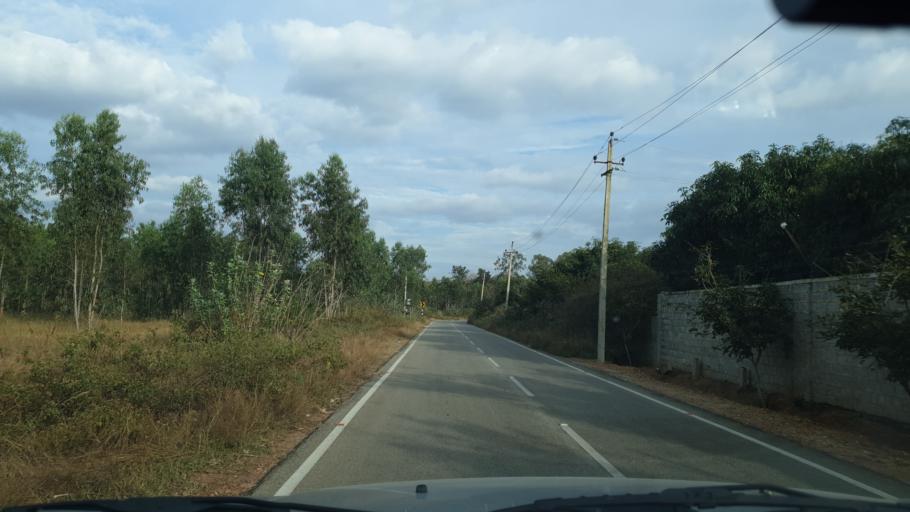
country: IN
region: Karnataka
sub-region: Bangalore Urban
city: Yelahanka
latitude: 13.2020
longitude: 77.6077
